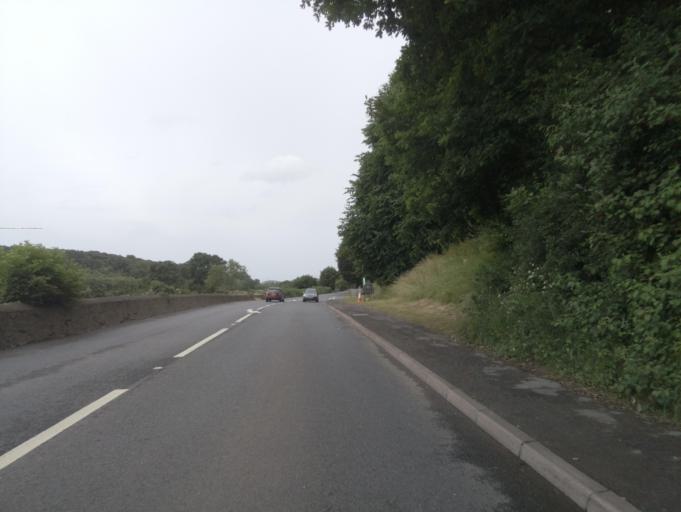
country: GB
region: England
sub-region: Devon
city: Chudleigh
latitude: 50.5931
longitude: -3.6173
